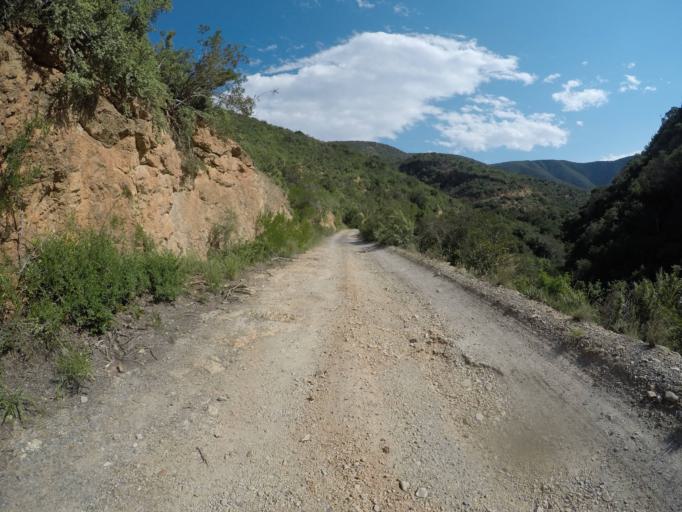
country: ZA
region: Eastern Cape
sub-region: Cacadu District Municipality
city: Kareedouw
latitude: -33.6555
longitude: 24.3610
